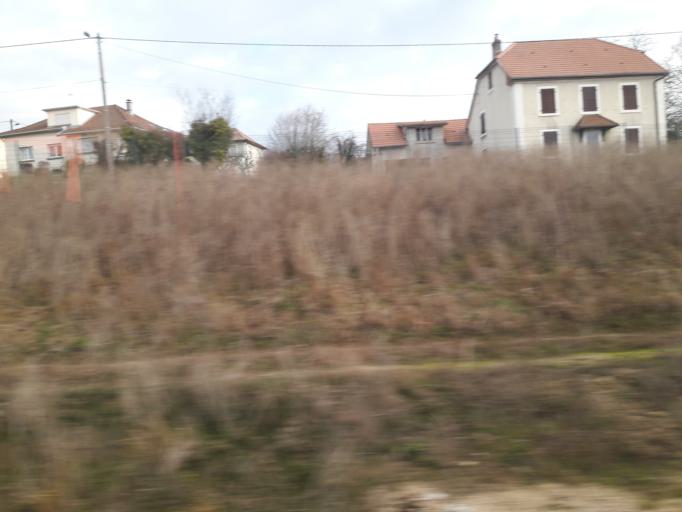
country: FR
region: Franche-Comte
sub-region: Territoire de Belfort
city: Delle
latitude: 47.5083
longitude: 7.0076
